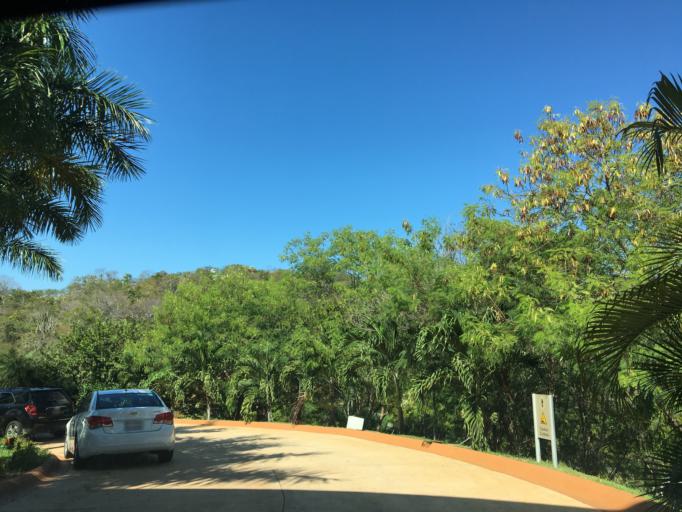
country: MX
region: Oaxaca
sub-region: Santa Maria Huatulco
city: Crucecita
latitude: 15.7831
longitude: -96.0657
